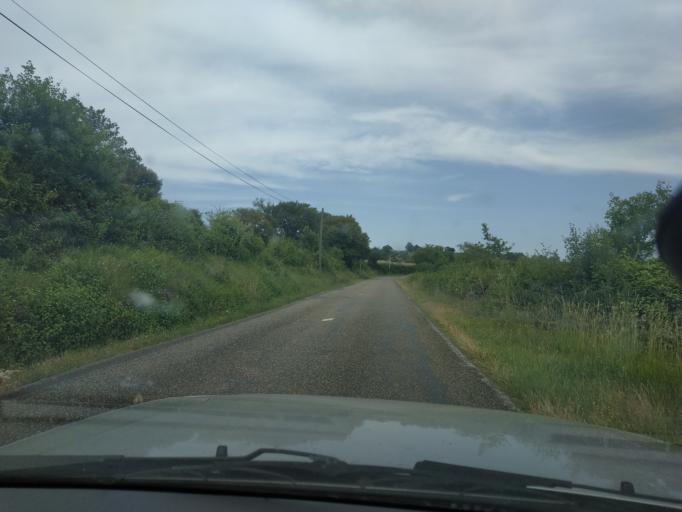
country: FR
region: Midi-Pyrenees
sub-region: Departement du Lot
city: Gramat
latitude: 44.6056
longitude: 1.6468
